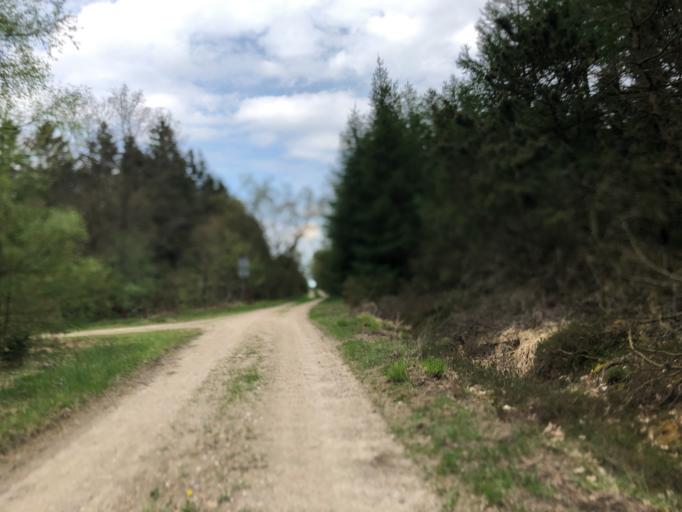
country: DK
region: Central Jutland
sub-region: Holstebro Kommune
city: Ulfborg
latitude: 56.2914
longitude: 8.4283
